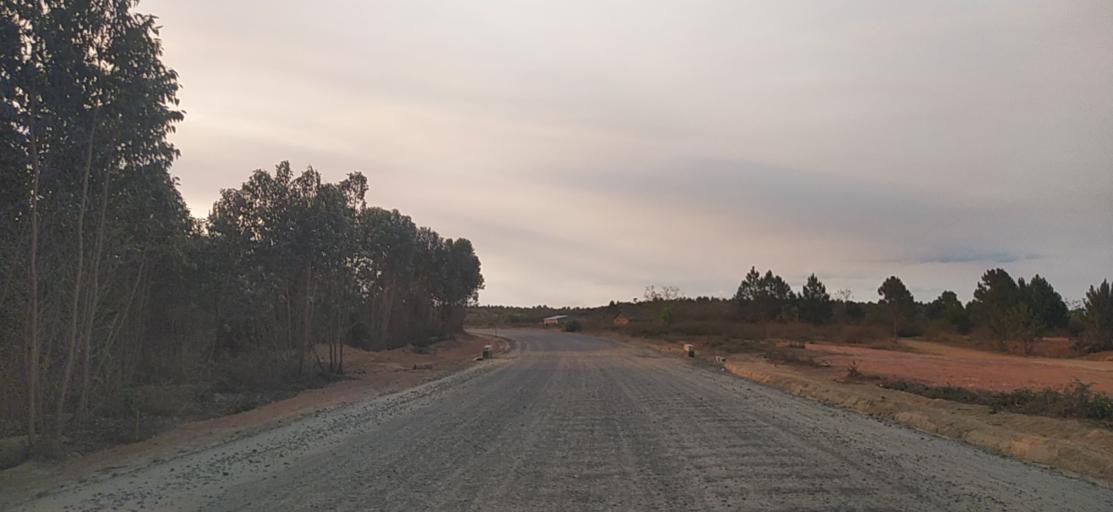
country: MG
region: Analamanga
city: Anjozorobe
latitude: -18.5007
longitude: 48.2677
